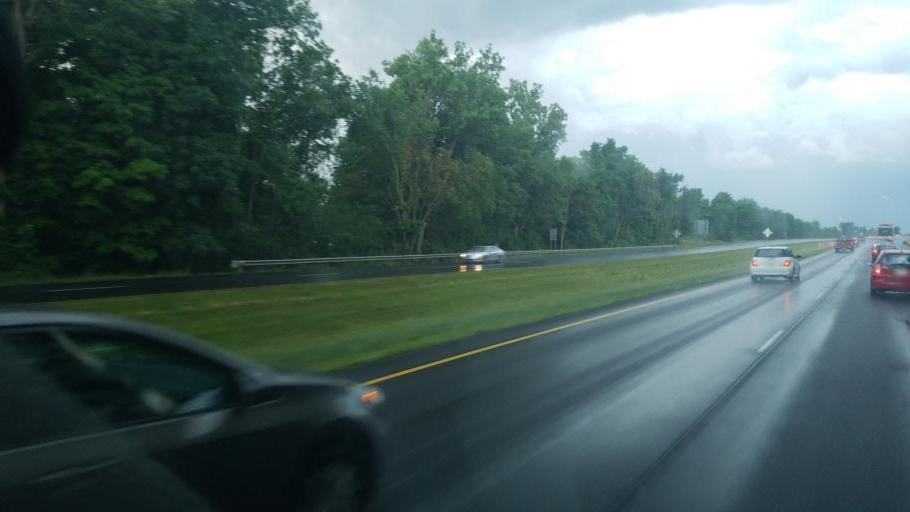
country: US
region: Ohio
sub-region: Summit County
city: Montrose-Ghent
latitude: 41.1049
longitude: -81.6562
